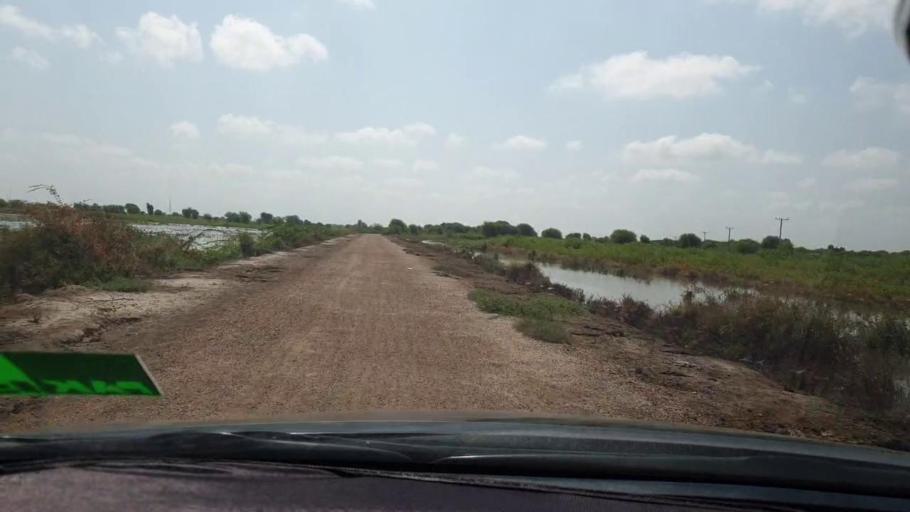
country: PK
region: Sindh
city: Tando Bago
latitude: 24.9397
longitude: 69.0924
